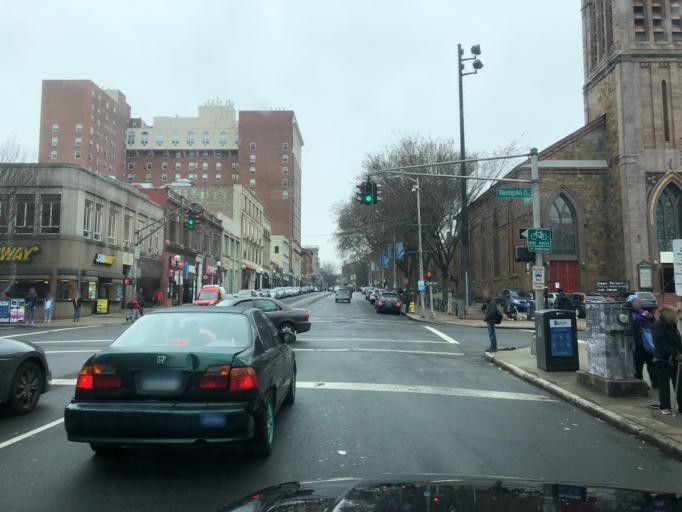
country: US
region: Connecticut
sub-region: New Haven County
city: New Haven
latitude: 41.3065
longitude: -72.9267
